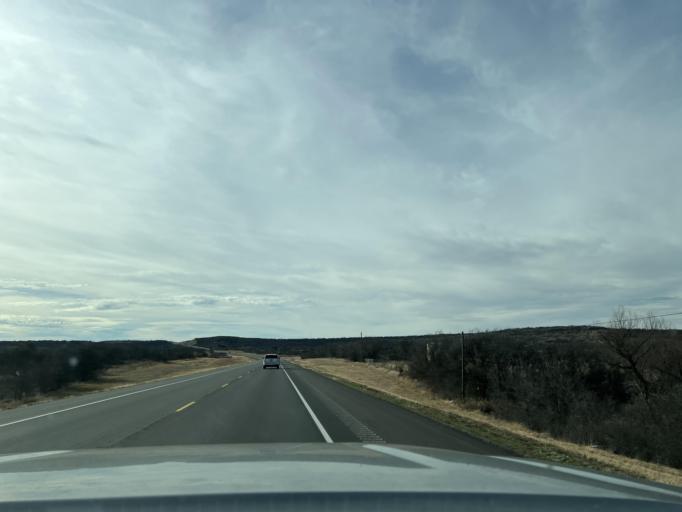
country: US
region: Texas
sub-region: Shackelford County
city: Albany
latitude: 32.7127
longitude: -99.3550
